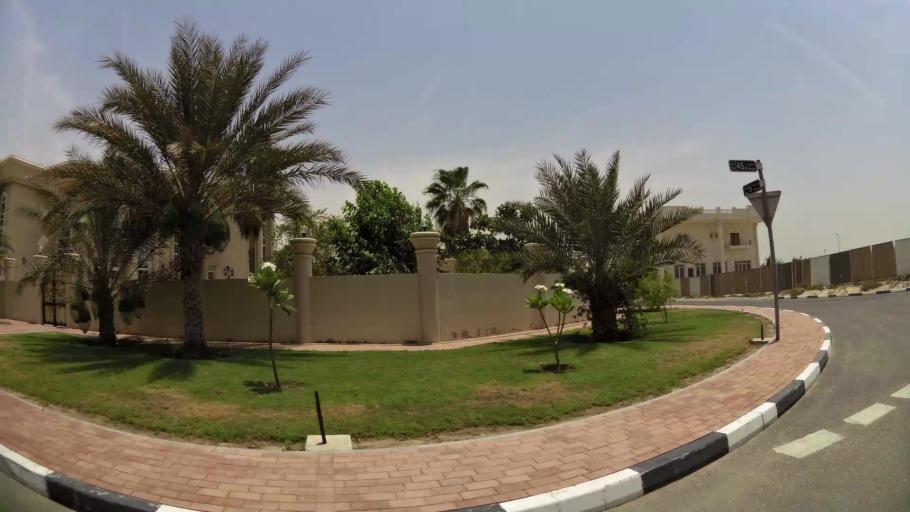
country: AE
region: Ash Shariqah
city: Sharjah
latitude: 25.2016
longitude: 55.3823
